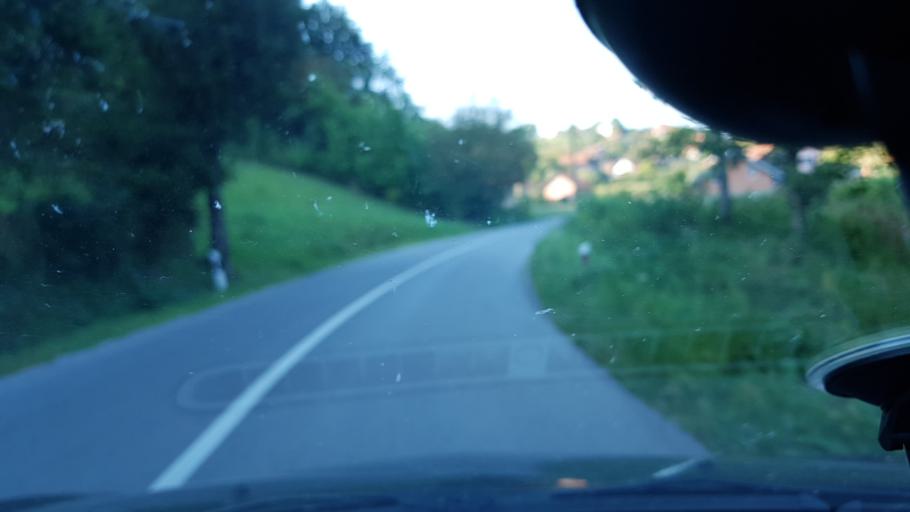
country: SI
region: Bistrica ob Sotli
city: Bistrica ob Sotli
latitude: 46.0558
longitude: 15.7707
